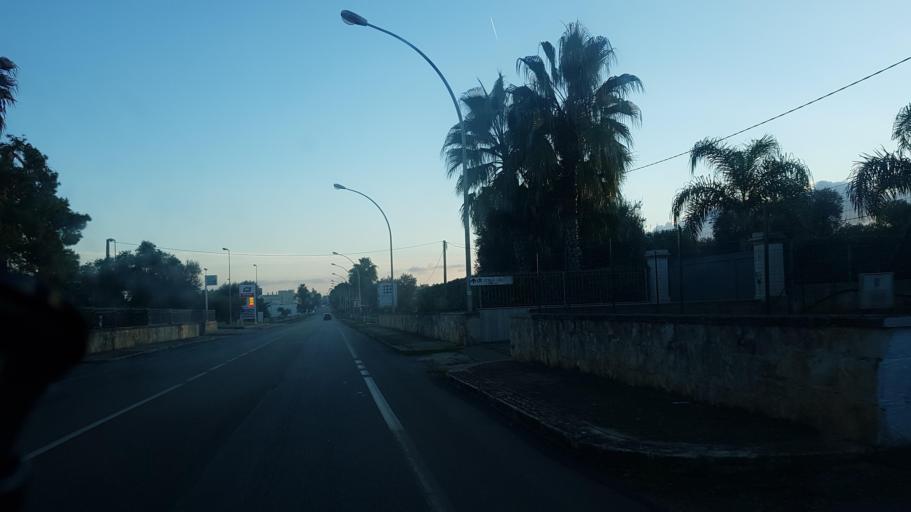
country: IT
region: Apulia
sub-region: Provincia di Brindisi
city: San Michele Salentino
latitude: 40.6402
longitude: 17.6320
